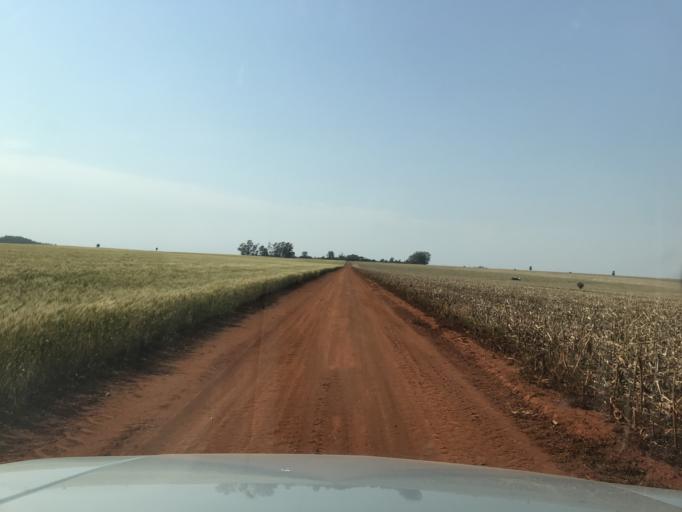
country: BR
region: Parana
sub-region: Palotina
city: Palotina
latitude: -24.2425
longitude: -53.7202
